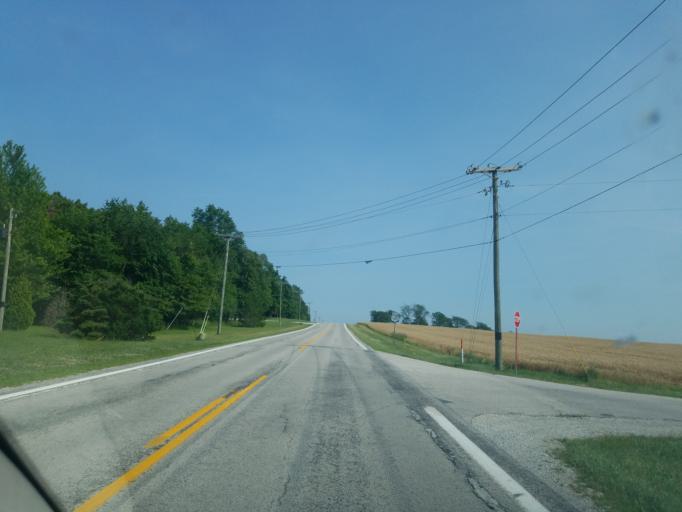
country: US
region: Ohio
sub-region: Wyandot County
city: Carey
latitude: 41.0145
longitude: -83.2855
